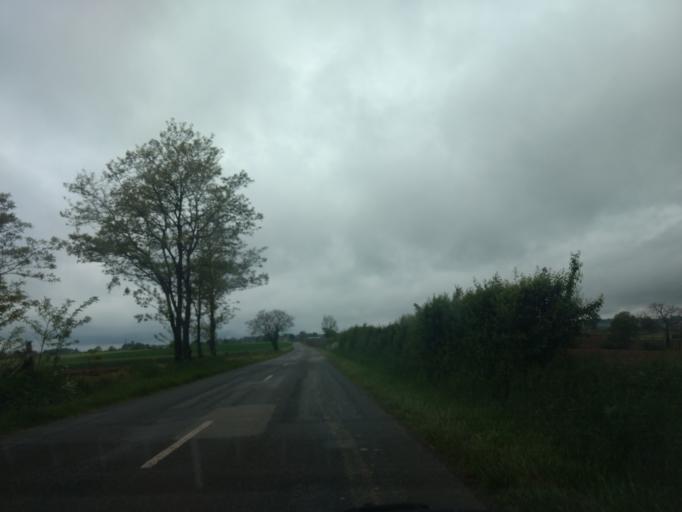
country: FR
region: Midi-Pyrenees
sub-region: Departement de l'Aveyron
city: Viviez
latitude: 44.5192
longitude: 2.1814
